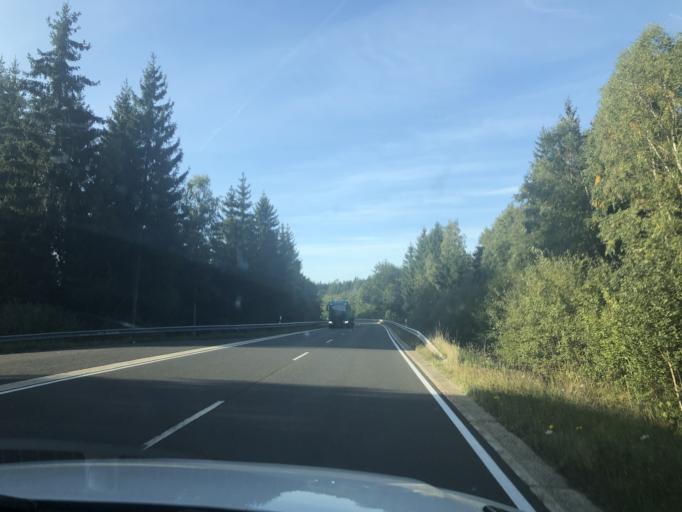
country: DE
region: Rheinland-Pfalz
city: Reinsfeld
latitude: 49.6989
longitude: 6.8528
